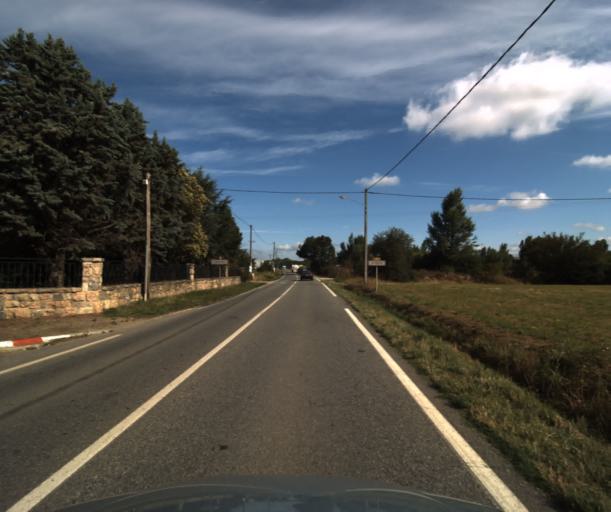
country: FR
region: Midi-Pyrenees
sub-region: Departement de la Haute-Garonne
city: Seysses
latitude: 43.4860
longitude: 1.3185
